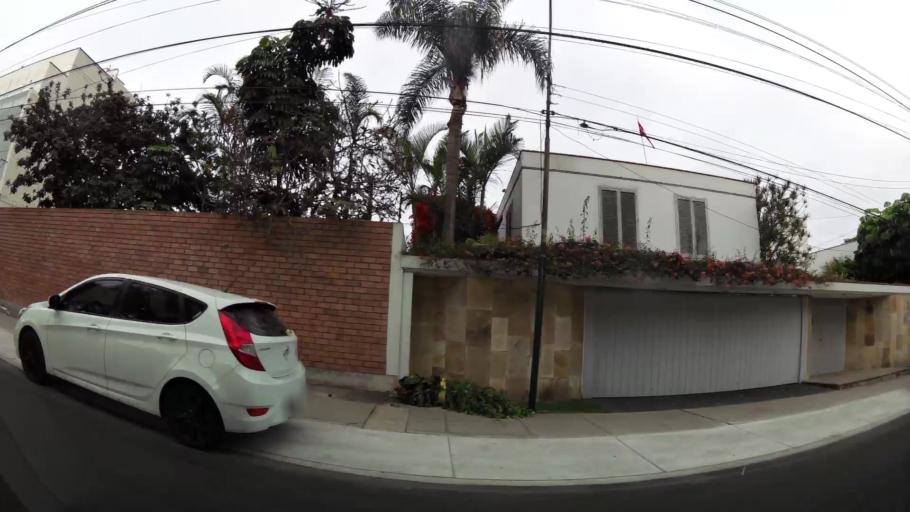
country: PE
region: Lima
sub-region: Lima
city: San Isidro
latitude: -12.1067
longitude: -77.0527
